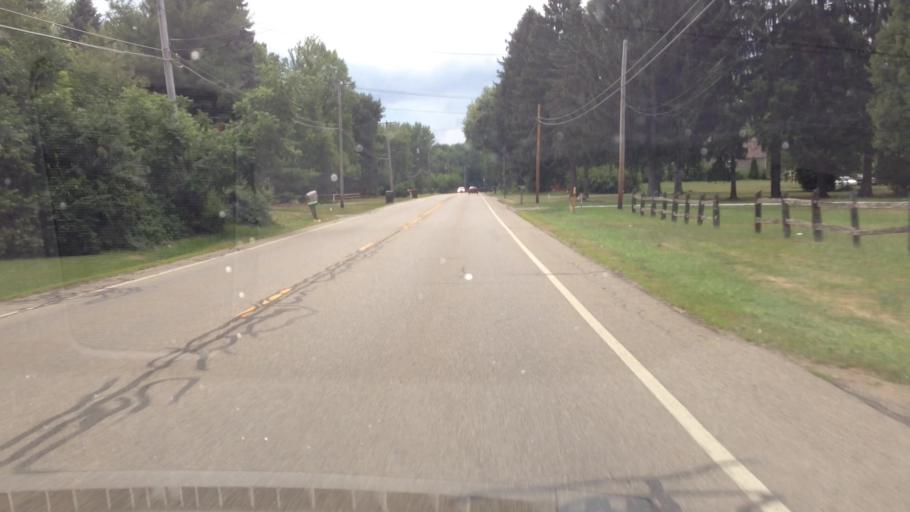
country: US
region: Ohio
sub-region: Summit County
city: Green
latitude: 40.9740
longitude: -81.4573
